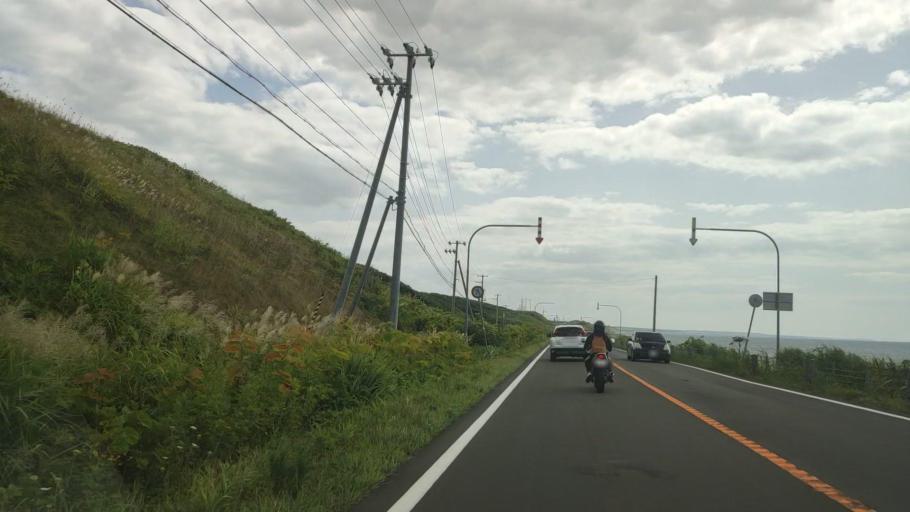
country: JP
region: Hokkaido
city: Rumoi
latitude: 44.5085
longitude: 141.7648
